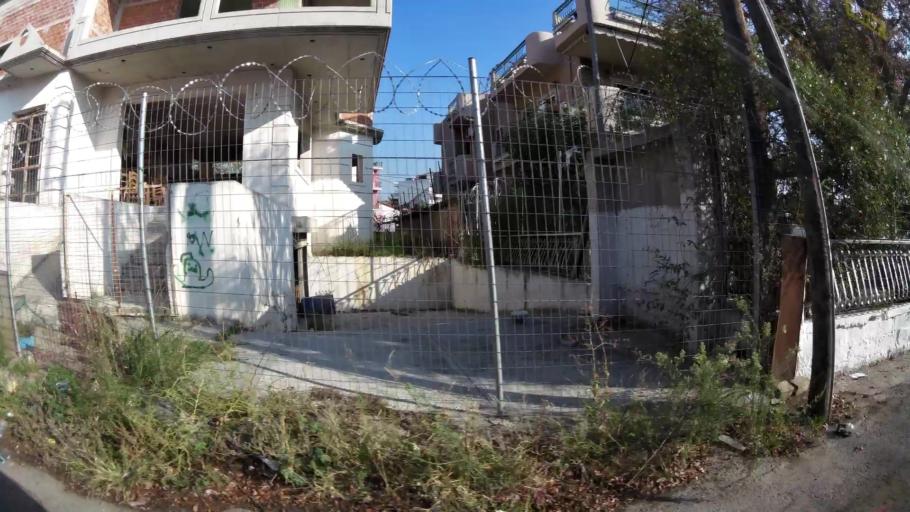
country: GR
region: Attica
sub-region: Nomarchia Anatolikis Attikis
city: Acharnes
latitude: 38.0780
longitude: 23.7236
